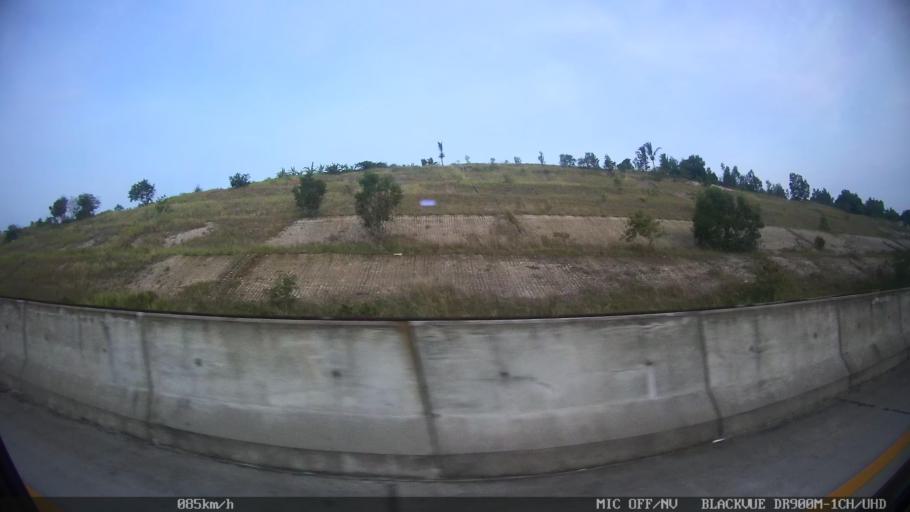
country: ID
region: Lampung
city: Penengahan
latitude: -5.8267
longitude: 105.7337
